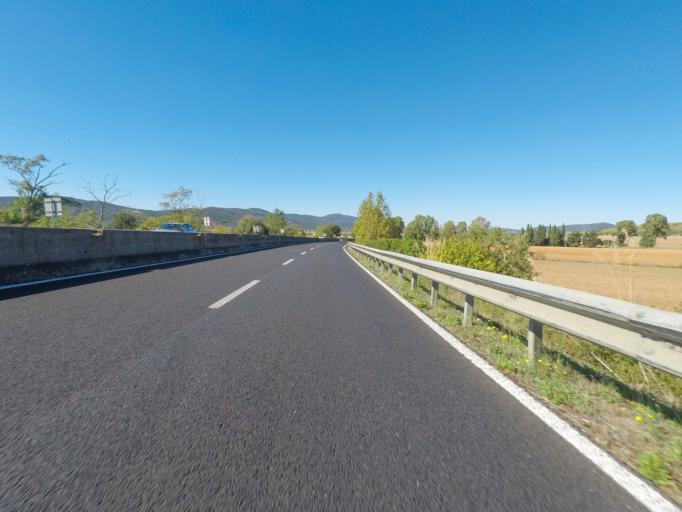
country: IT
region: Tuscany
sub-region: Provincia di Grosseto
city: Fonteblanda
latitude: 42.5694
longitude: 11.1696
